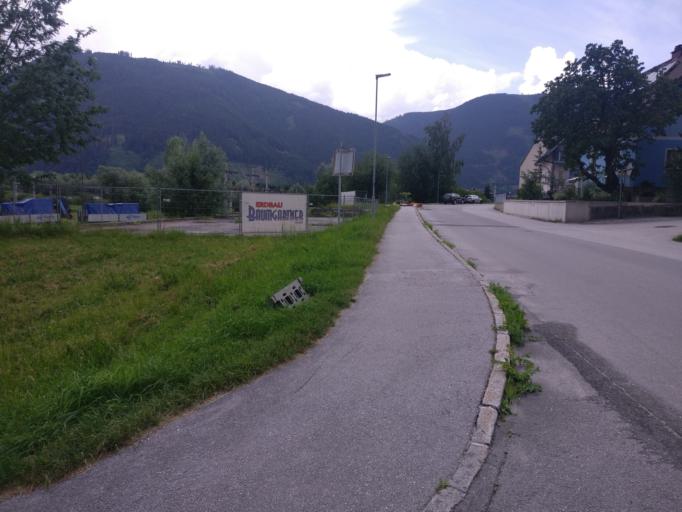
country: AT
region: Styria
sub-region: Politischer Bezirk Liezen
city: Selzthal
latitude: 47.5554
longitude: 14.3222
